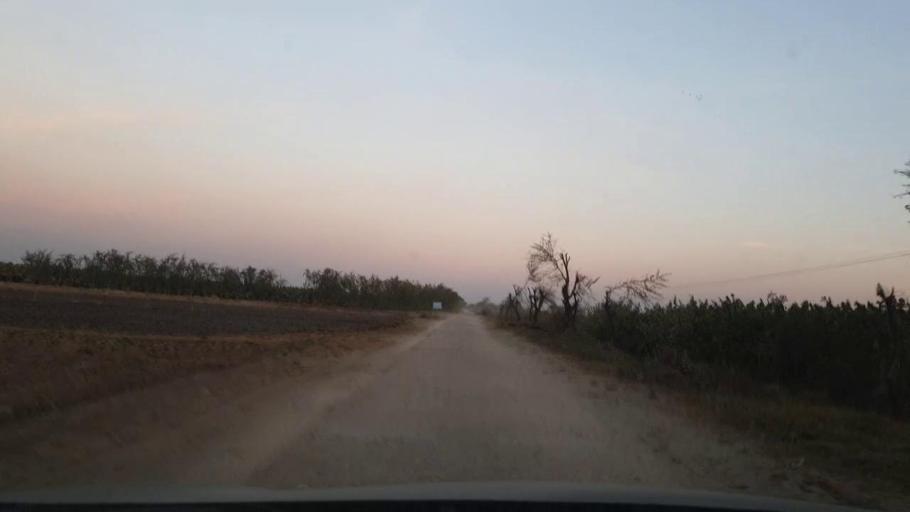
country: PK
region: Sindh
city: Tando Allahyar
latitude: 25.5582
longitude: 68.7792
